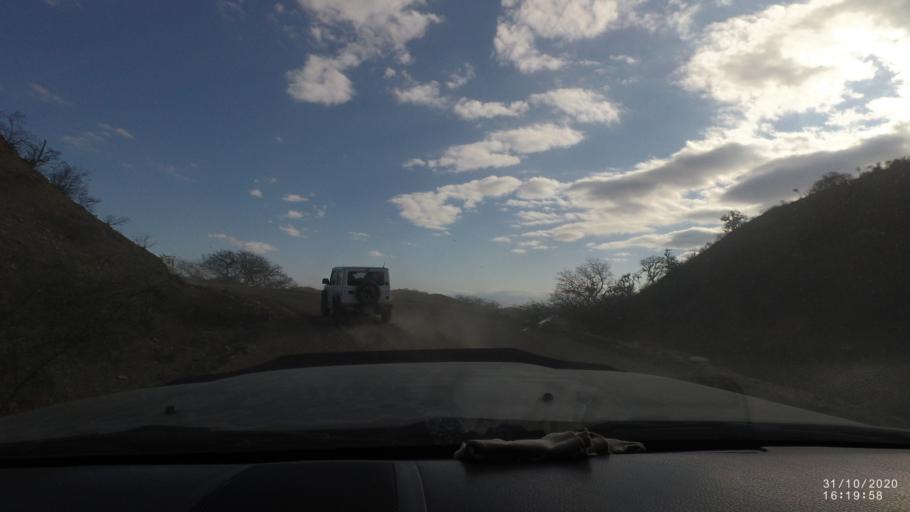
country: BO
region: Chuquisaca
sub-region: Provincia Zudanez
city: Mojocoya
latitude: -18.3976
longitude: -64.6033
